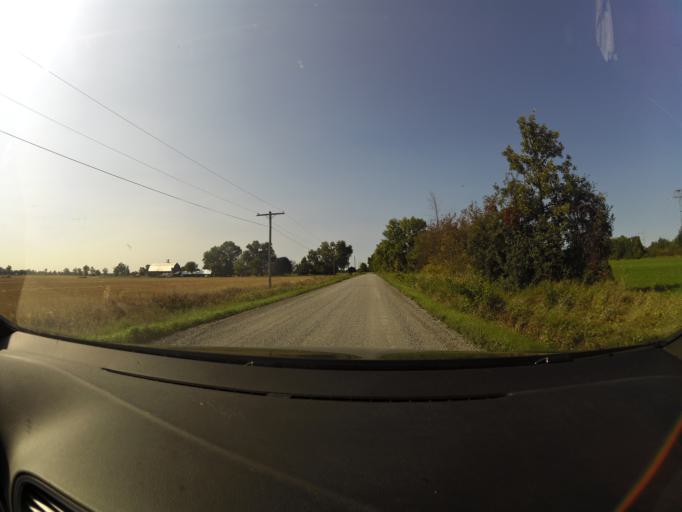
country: CA
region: Ontario
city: Arnprior
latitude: 45.3847
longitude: -76.3233
